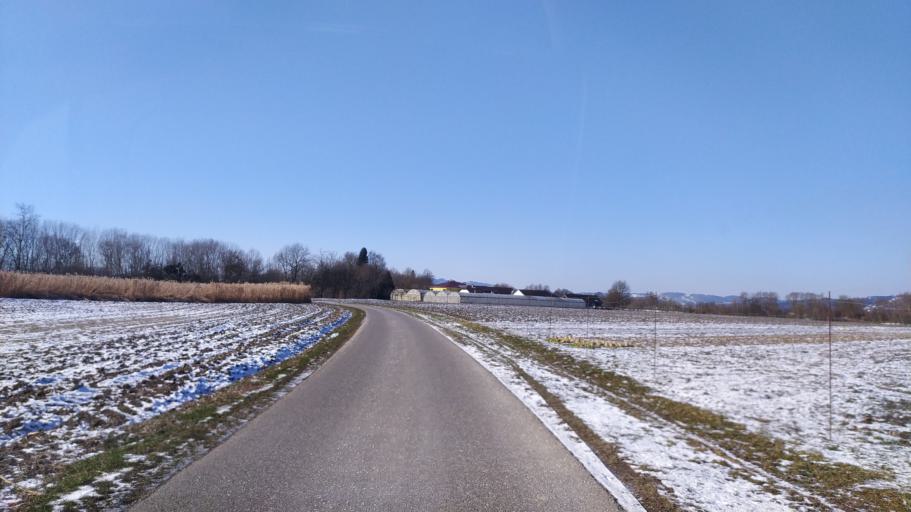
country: AT
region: Upper Austria
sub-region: Politischer Bezirk Urfahr-Umgebung
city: Goldworth
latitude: 48.3335
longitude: 14.0855
